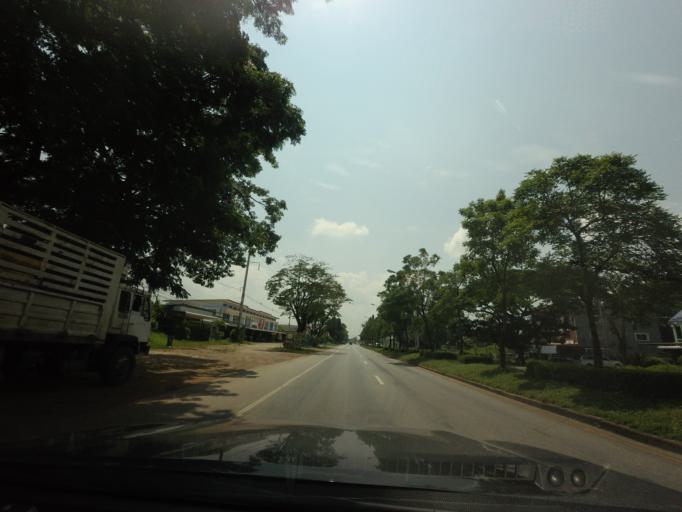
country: TH
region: Uttaradit
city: Uttaradit
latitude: 17.6173
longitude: 100.1241
